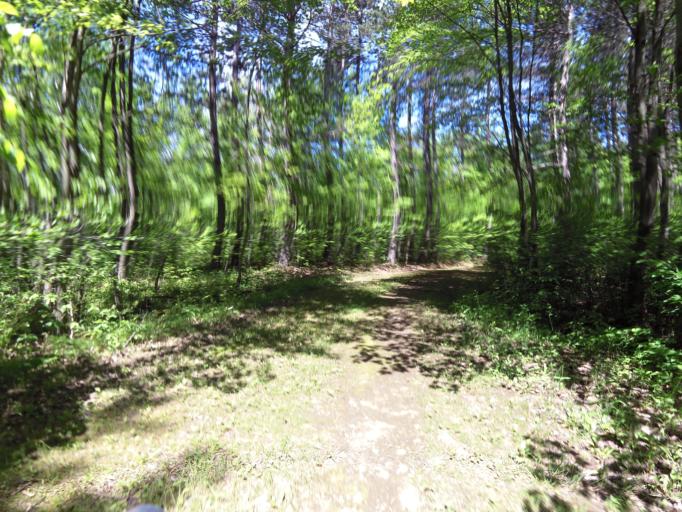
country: CA
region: Ontario
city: Ottawa
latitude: 45.3525
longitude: -75.6043
